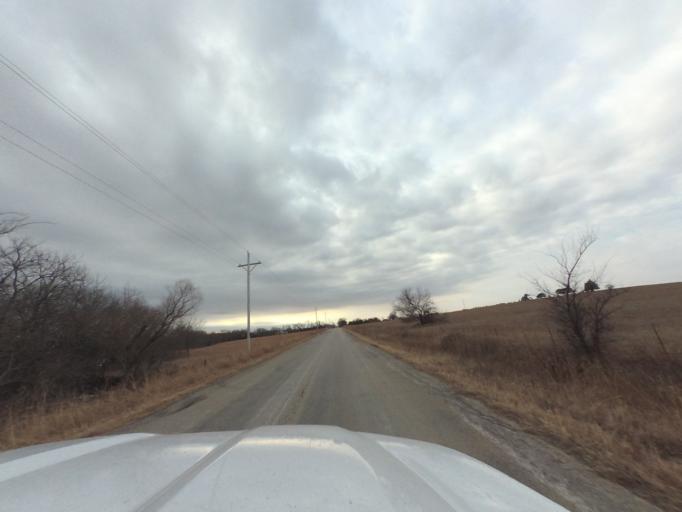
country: US
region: Kansas
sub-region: Chase County
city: Cottonwood Falls
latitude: 38.4331
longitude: -96.3732
